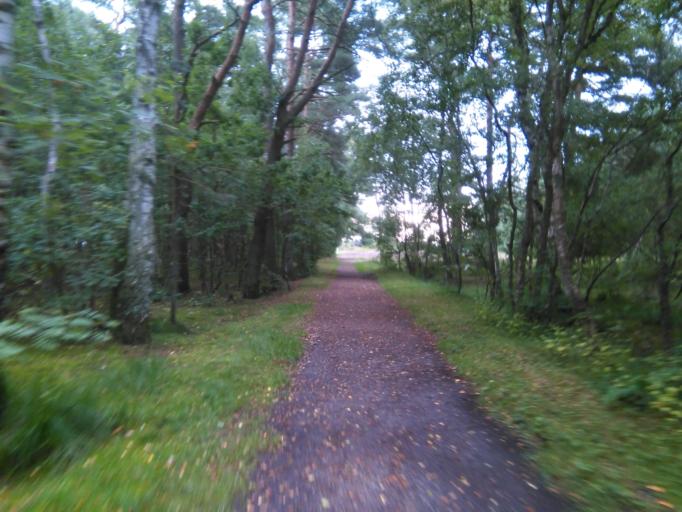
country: DK
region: Central Jutland
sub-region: Arhus Kommune
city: Logten
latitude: 56.2378
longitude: 10.3353
